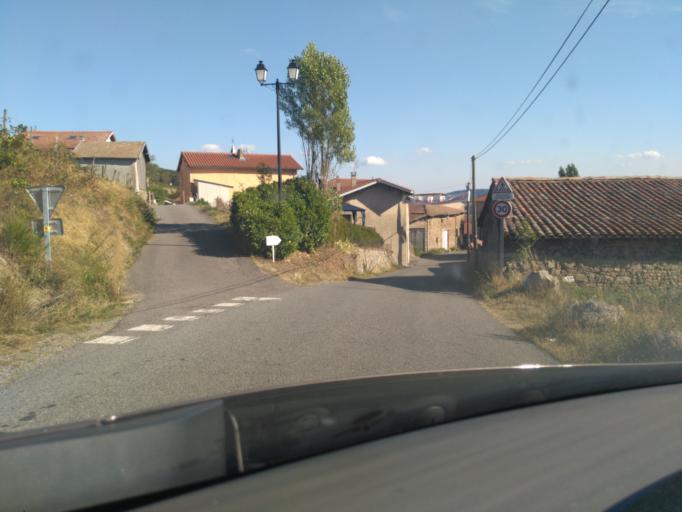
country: FR
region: Rhone-Alpes
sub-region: Departement de la Loire
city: Violay
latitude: 45.8452
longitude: 4.4018
